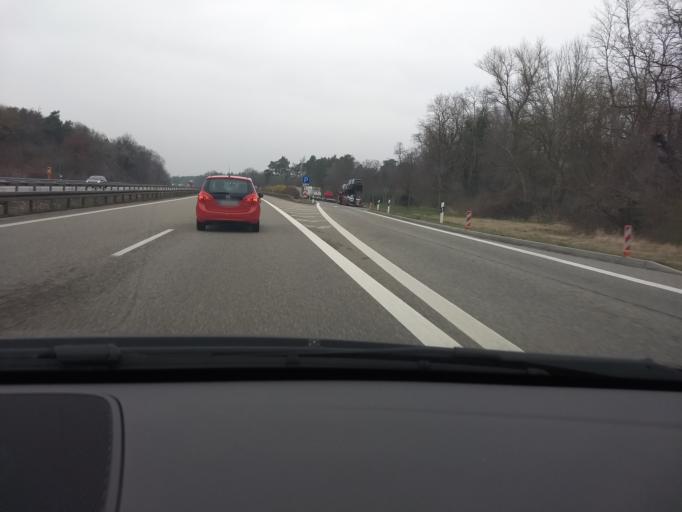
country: DE
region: Baden-Wuerttemberg
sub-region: Freiburg Region
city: Bad Bellingen
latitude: 47.7445
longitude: 7.5516
